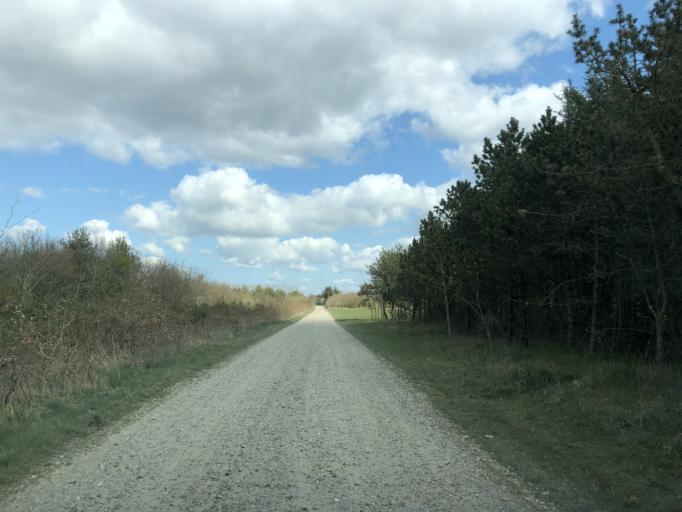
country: DK
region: Central Jutland
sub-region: Holstebro Kommune
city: Ulfborg
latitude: 56.3770
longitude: 8.2094
